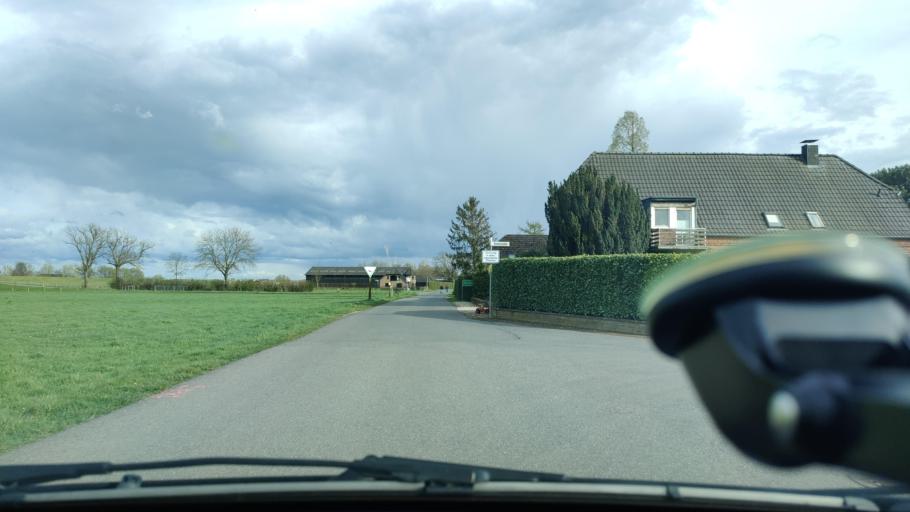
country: DE
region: North Rhine-Westphalia
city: Rees
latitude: 51.7382
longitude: 6.4061
